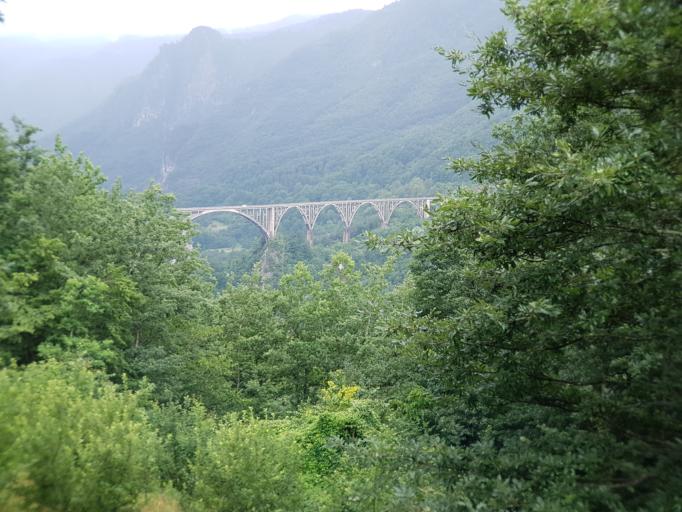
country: ME
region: Opstina Zabljak
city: Zabljak
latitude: 43.1588
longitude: 19.2926
